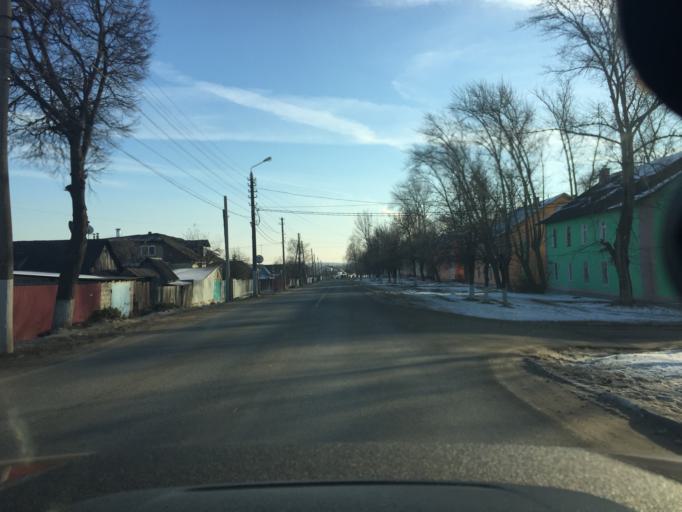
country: RU
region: Tula
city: Tula
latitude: 54.1840
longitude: 37.7065
